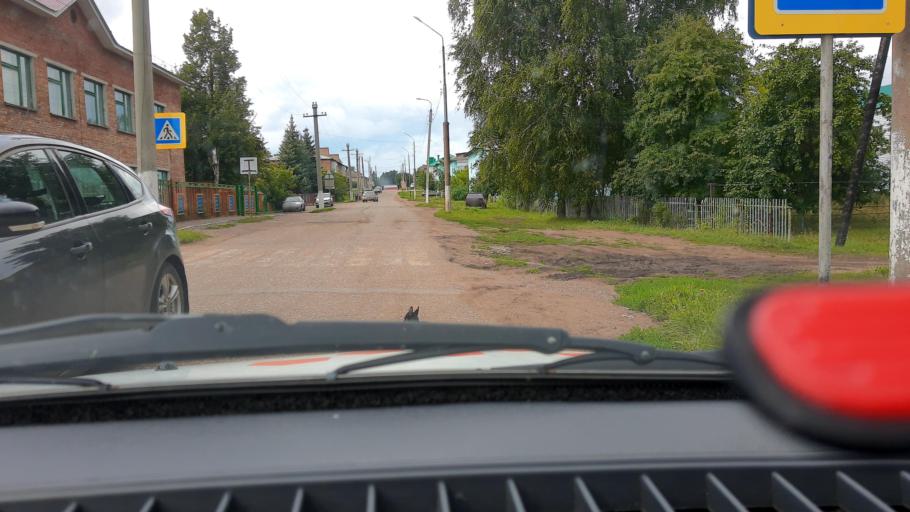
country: RU
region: Bashkortostan
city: Semiletka
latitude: 55.3594
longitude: 54.6154
